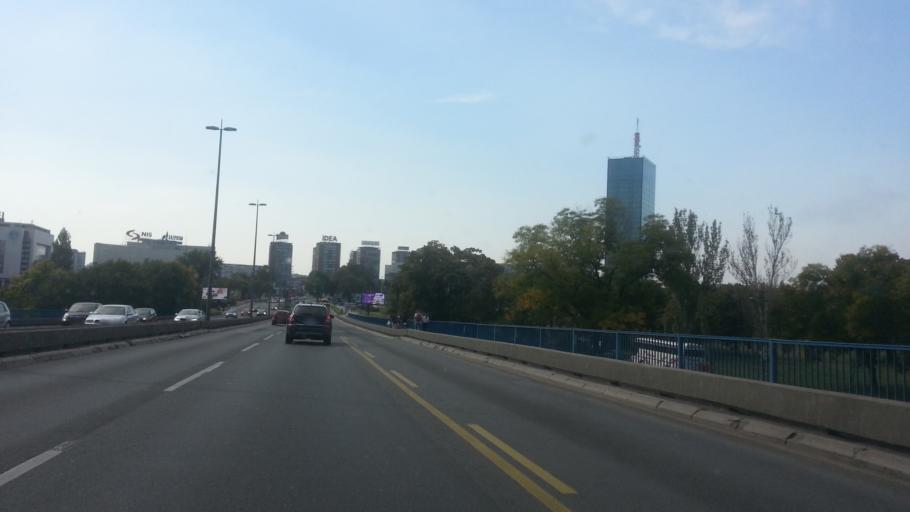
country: RS
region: Central Serbia
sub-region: Belgrade
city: Stari Grad
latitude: 44.8147
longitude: 20.4436
